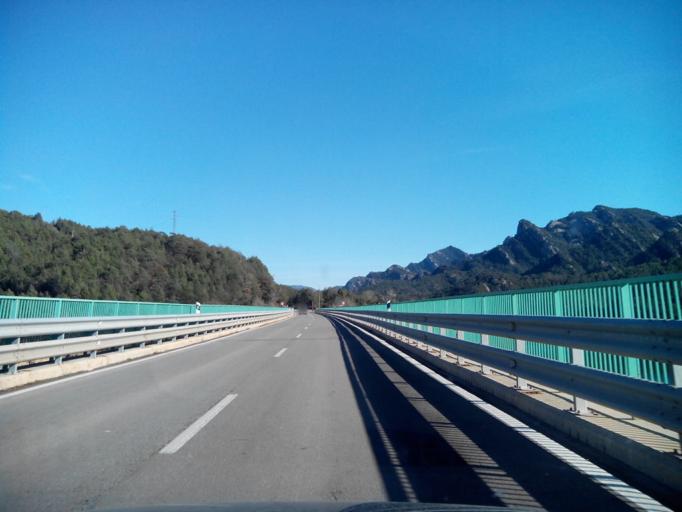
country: ES
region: Catalonia
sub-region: Provincia de Barcelona
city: Berga
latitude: 42.1269
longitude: 1.8810
